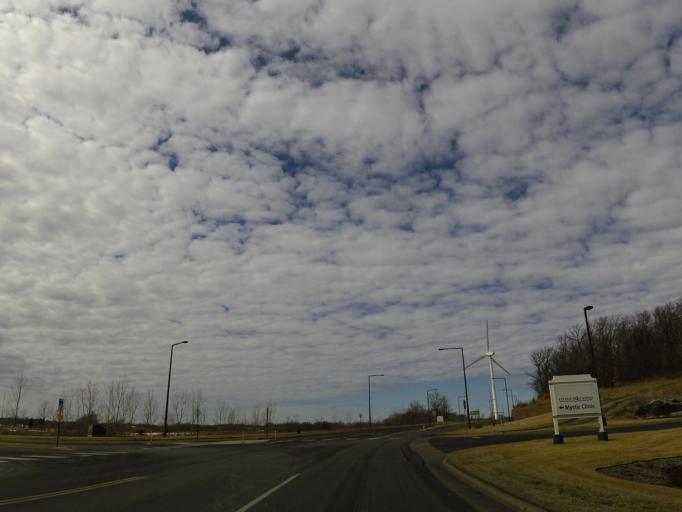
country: US
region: Minnesota
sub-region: Scott County
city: Prior Lake
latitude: 44.7356
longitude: -93.4760
